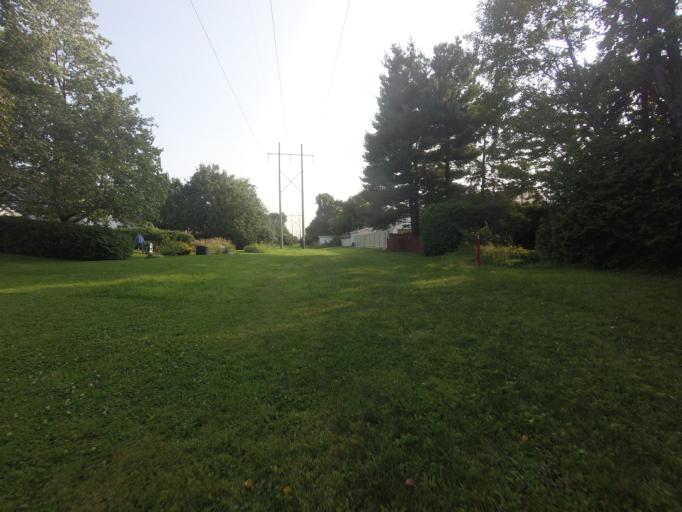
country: CA
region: Ontario
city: Bells Corners
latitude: 45.3320
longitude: -75.7766
